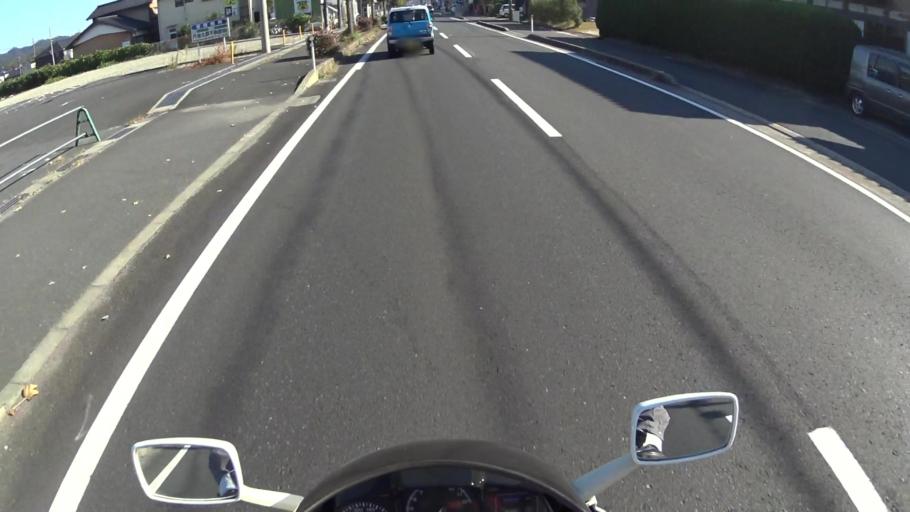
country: JP
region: Kyoto
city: Miyazu
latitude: 35.6031
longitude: 135.0847
